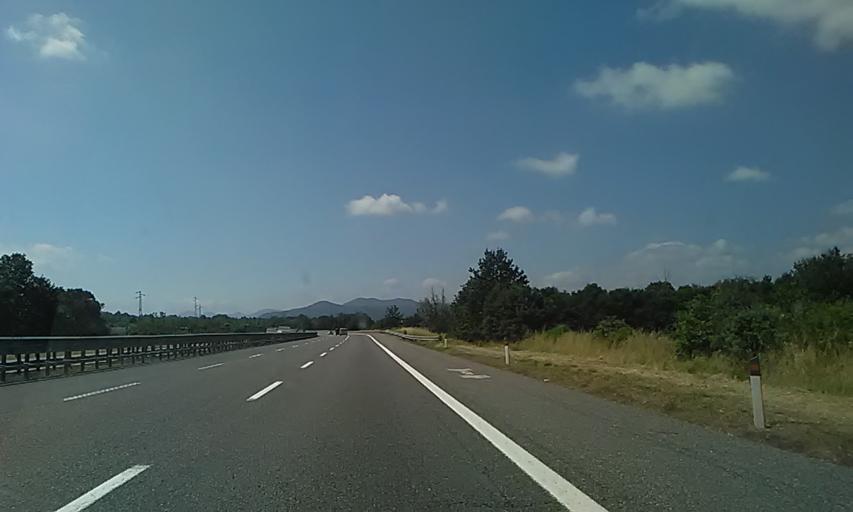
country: IT
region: Piedmont
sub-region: Provincia di Alessandria
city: Rocca Grimalda
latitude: 44.6643
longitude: 8.6592
